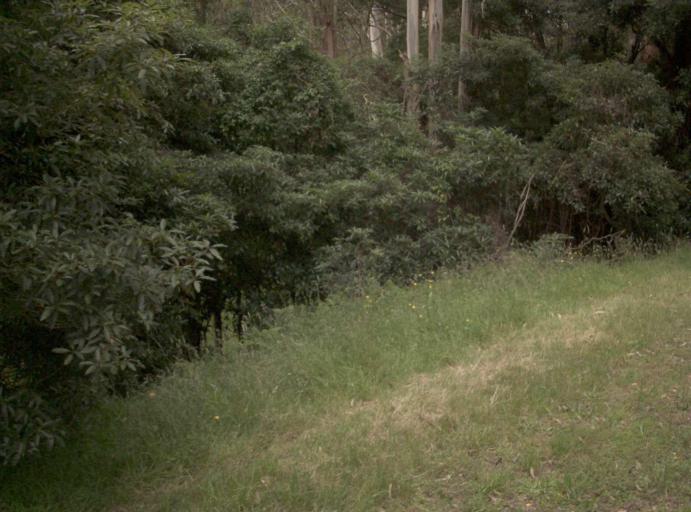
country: AU
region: Victoria
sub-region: Latrobe
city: Traralgon
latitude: -38.4809
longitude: 146.6018
